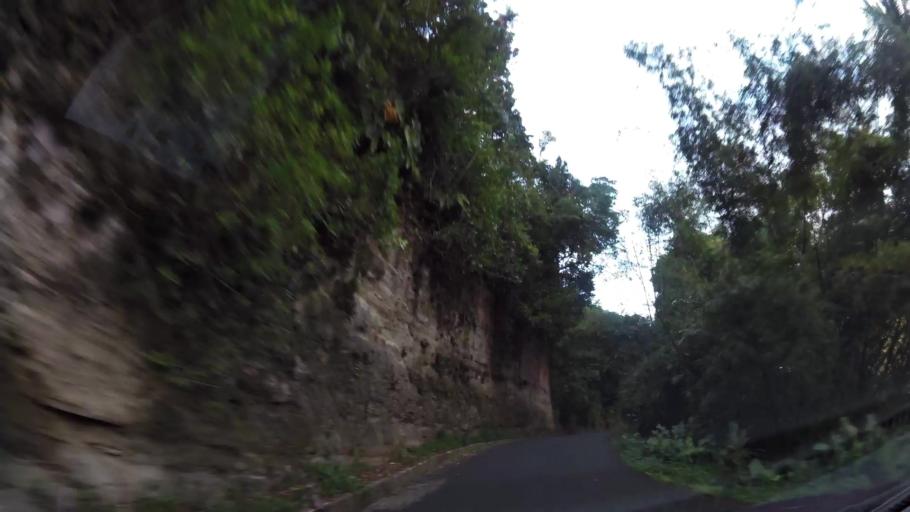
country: DM
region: Saint Andrew
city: Calibishie
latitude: 15.5882
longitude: -61.4016
